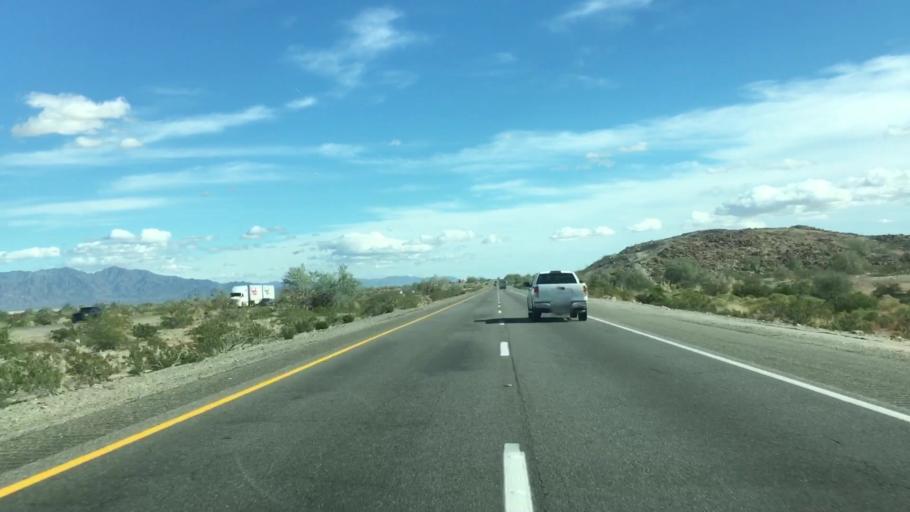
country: US
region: California
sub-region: Imperial County
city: Niland
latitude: 33.7071
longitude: -115.3529
